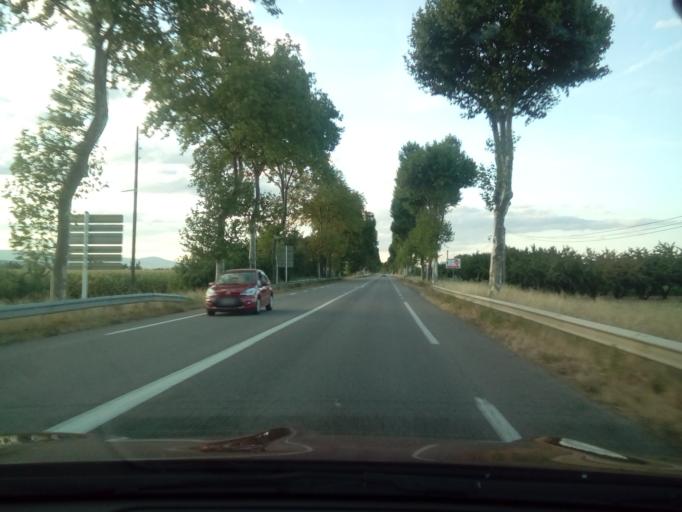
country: FR
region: Rhone-Alpes
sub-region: Departement de la Drome
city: Andancette
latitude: 45.2647
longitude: 4.8240
